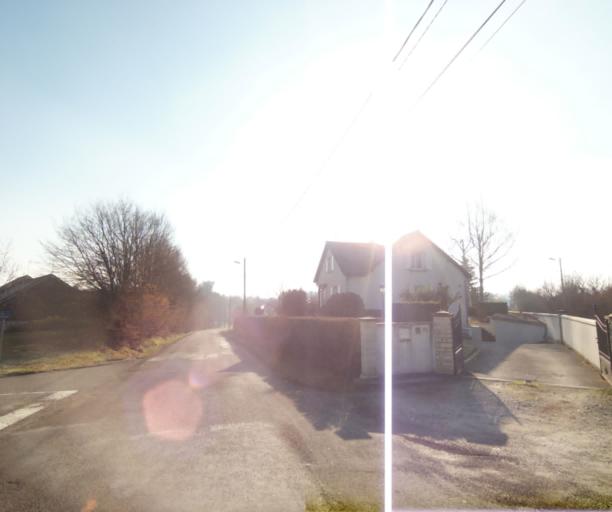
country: FR
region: Champagne-Ardenne
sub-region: Departement de la Haute-Marne
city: Wassy
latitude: 48.5028
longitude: 4.9569
